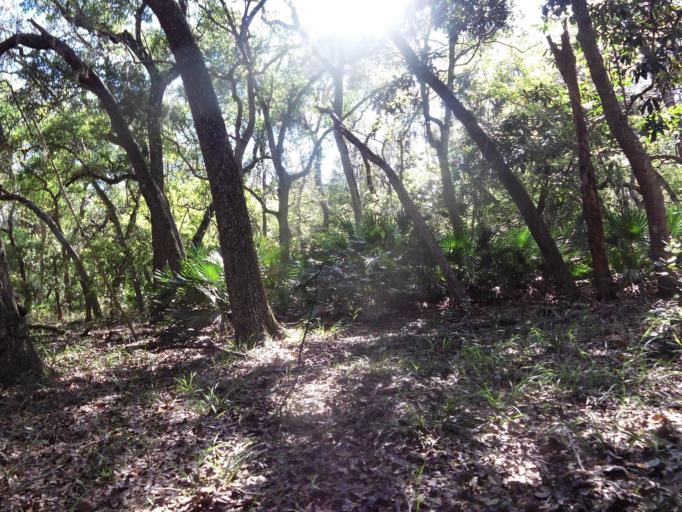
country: US
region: Florida
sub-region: Saint Johns County
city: Villano Beach
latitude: 29.9961
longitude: -81.3267
